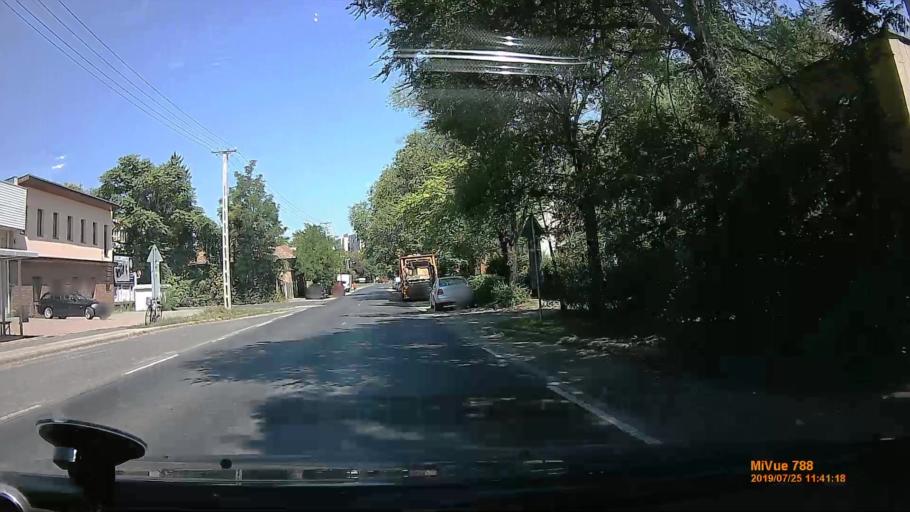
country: HU
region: Szabolcs-Szatmar-Bereg
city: Nyiregyhaza
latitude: 47.9395
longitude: 21.7130
